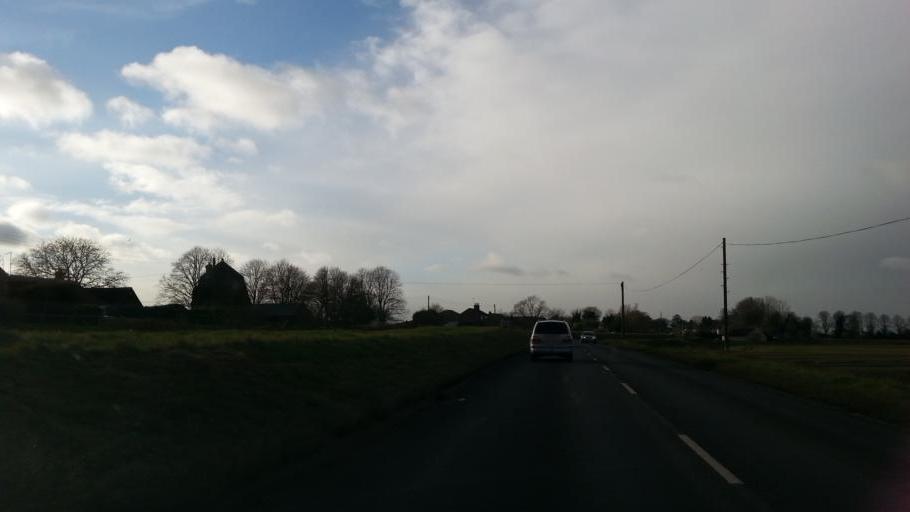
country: GB
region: England
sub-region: Norfolk
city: Outwell
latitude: 52.5842
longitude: 0.3040
